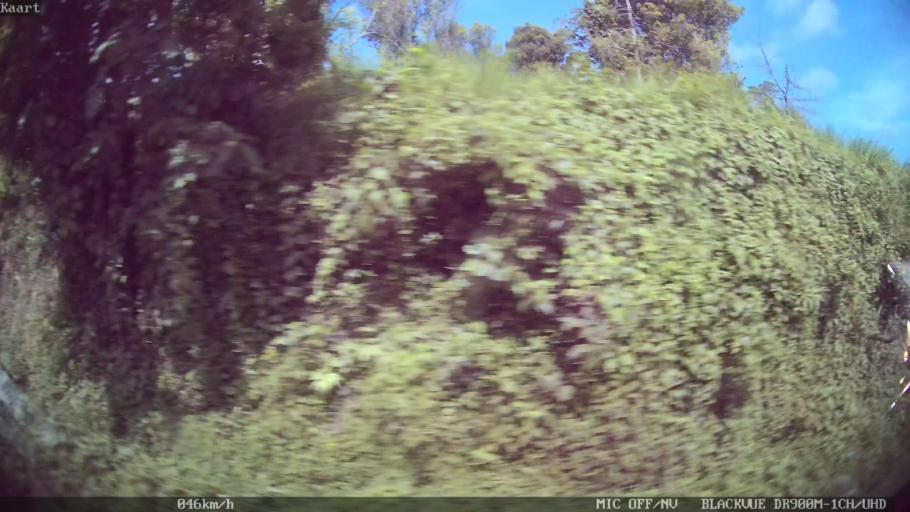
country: ID
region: Bali
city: Banjar Kelodan
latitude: -8.5233
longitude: 115.3293
